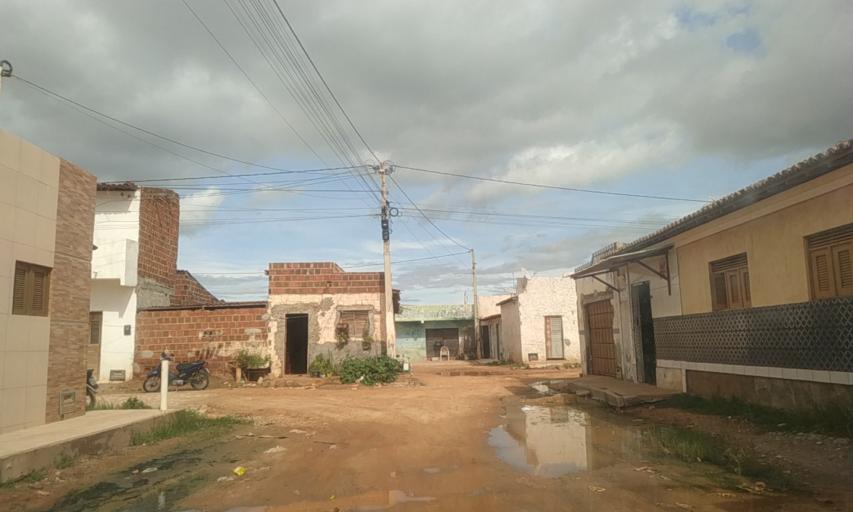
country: BR
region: Rio Grande do Norte
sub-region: Areia Branca
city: Areia Branca
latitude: -4.9531
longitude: -37.1209
